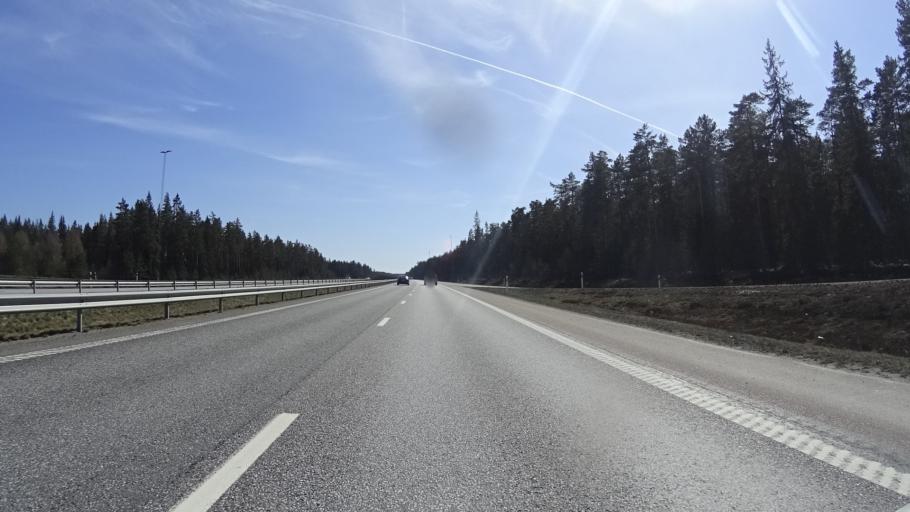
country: SE
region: Joenkoeping
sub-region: Vaggeryds Kommun
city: Skillingaryd
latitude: 57.3444
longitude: 14.1028
